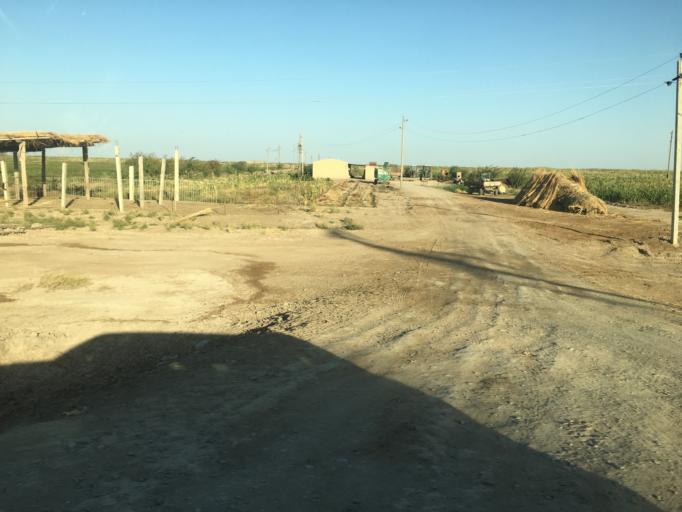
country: IR
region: Razavi Khorasan
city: Sarakhs
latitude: 37.1263
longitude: 61.2092
